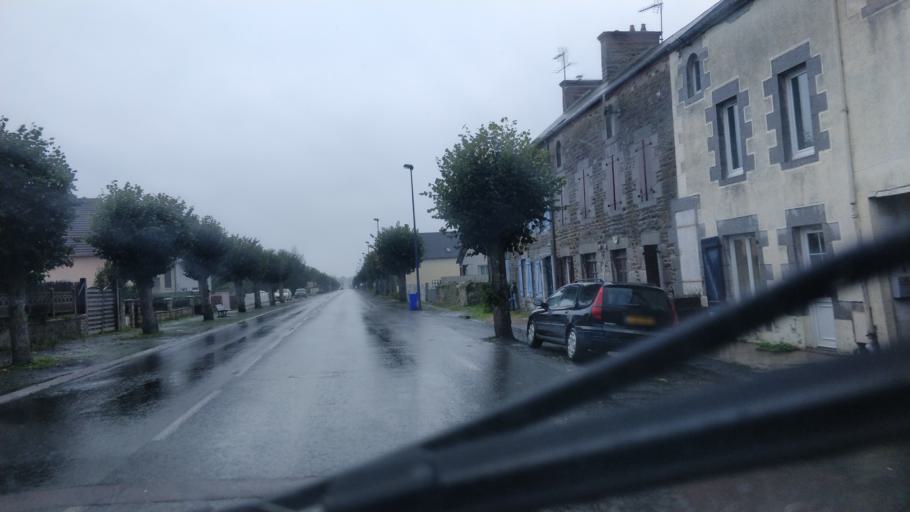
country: FR
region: Lower Normandy
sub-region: Departement de la Manche
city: Brehal
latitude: 48.8950
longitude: -1.5138
